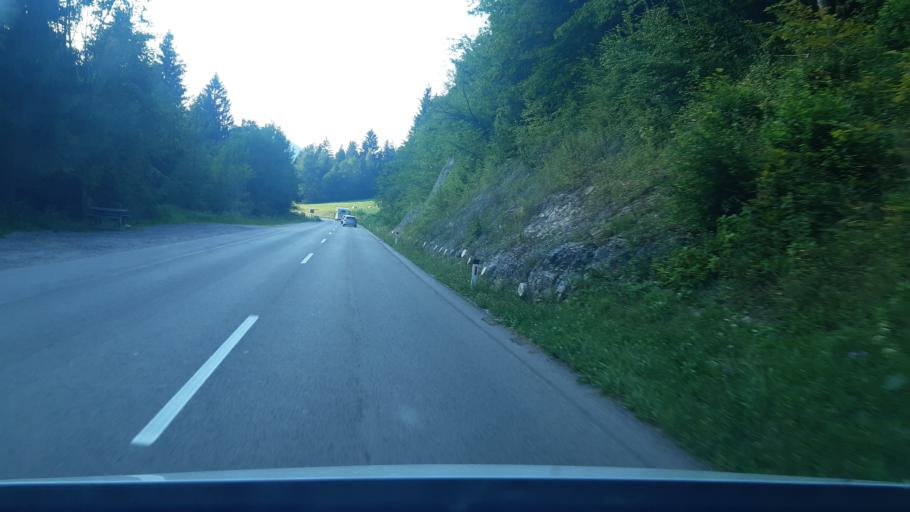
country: SI
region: Semic
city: Semic
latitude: 45.6602
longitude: 15.1148
